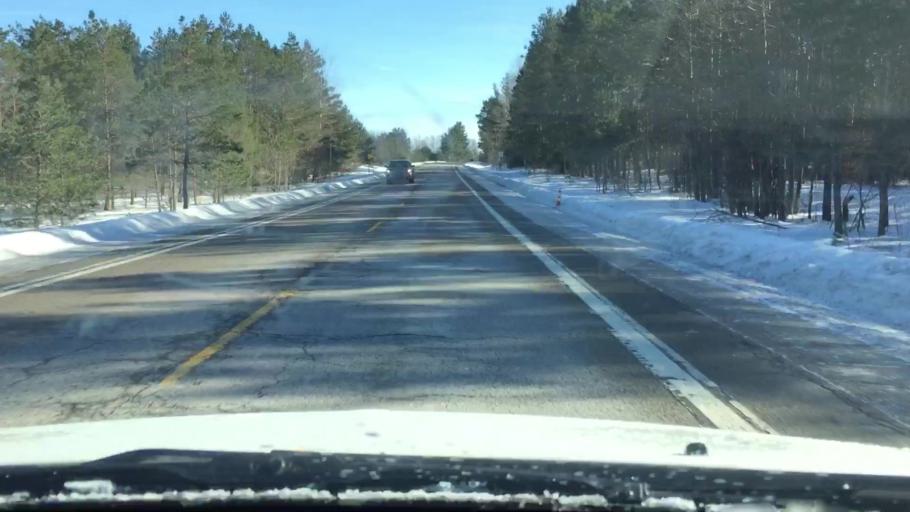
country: US
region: Michigan
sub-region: Charlevoix County
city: East Jordan
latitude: 45.0954
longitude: -85.1026
